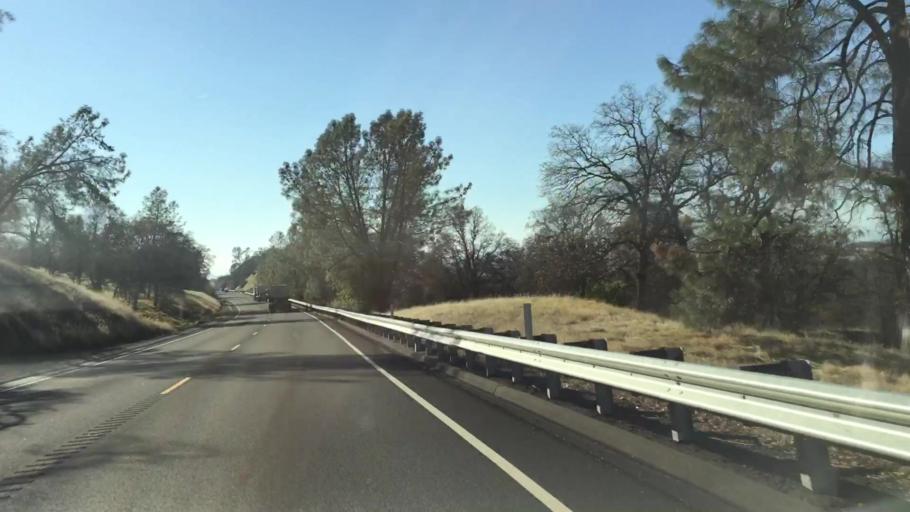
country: US
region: California
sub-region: Butte County
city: Paradise
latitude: 39.6454
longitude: -121.5666
